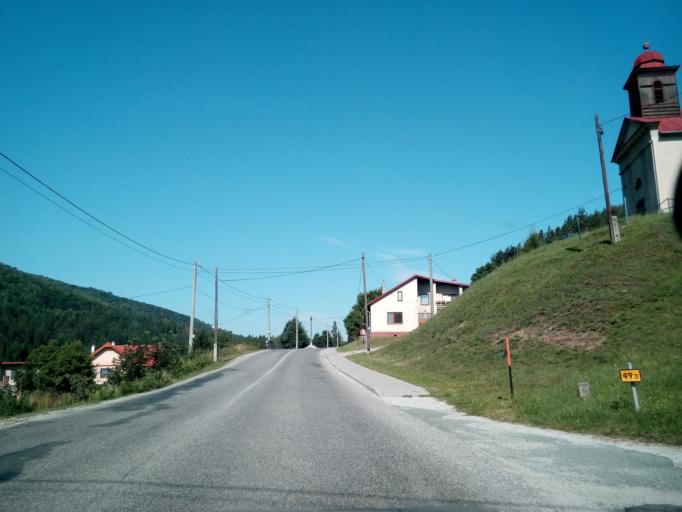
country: SK
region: Kosicky
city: Krompachy
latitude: 48.9284
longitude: 20.8506
